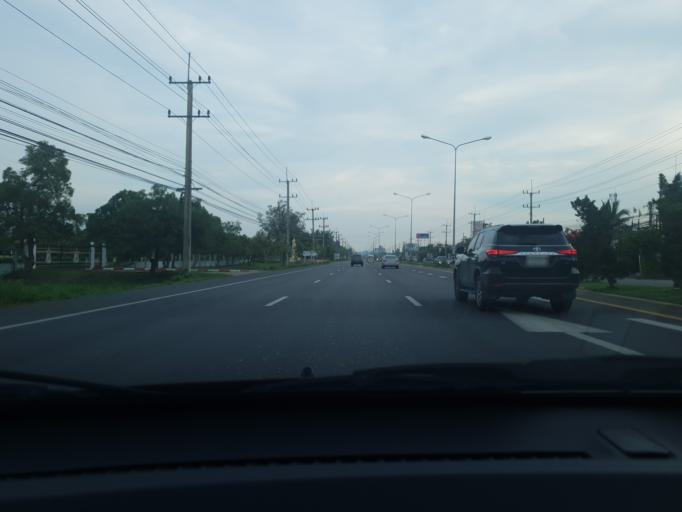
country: TH
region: Prachuap Khiri Khan
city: Hua Hin
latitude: 12.6802
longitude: 99.9528
